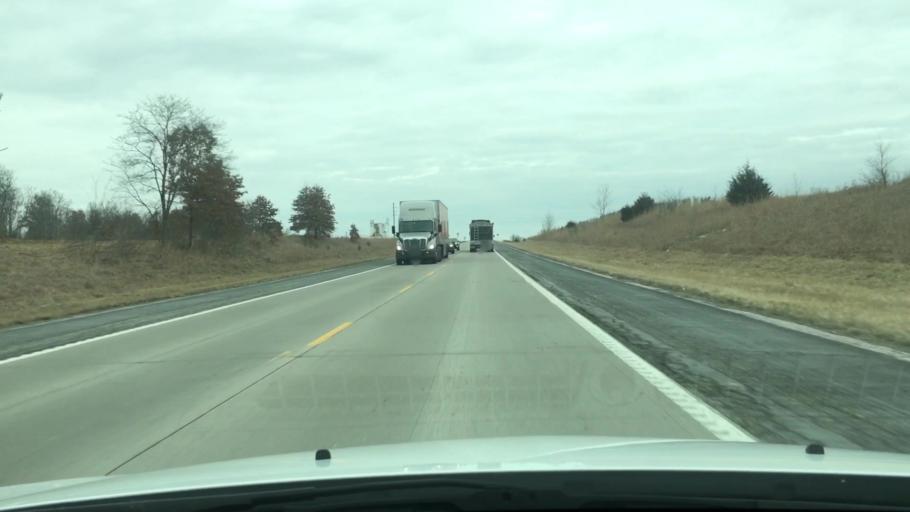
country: US
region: Missouri
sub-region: Audrain County
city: Mexico
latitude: 39.1510
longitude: -91.8435
